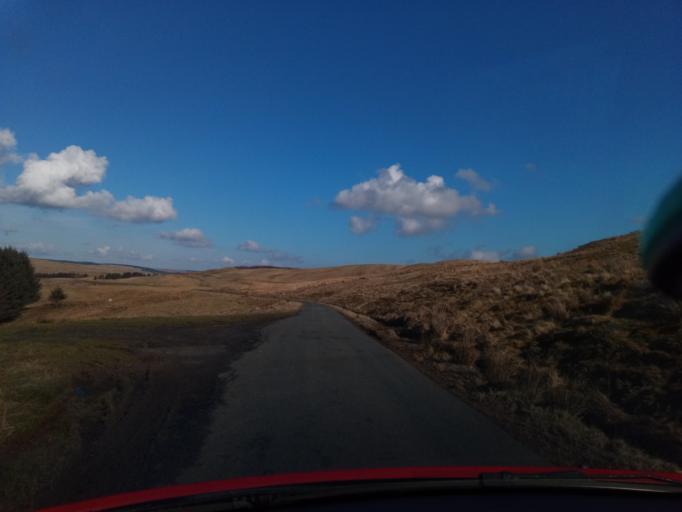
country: GB
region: Scotland
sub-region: The Scottish Borders
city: Hawick
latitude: 55.4481
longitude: -2.8867
